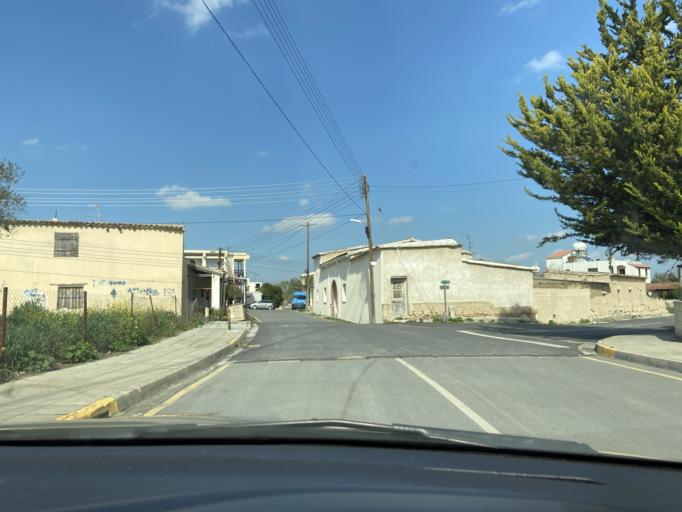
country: CY
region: Lefkosia
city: Alampra
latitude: 35.0127
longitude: 33.3880
